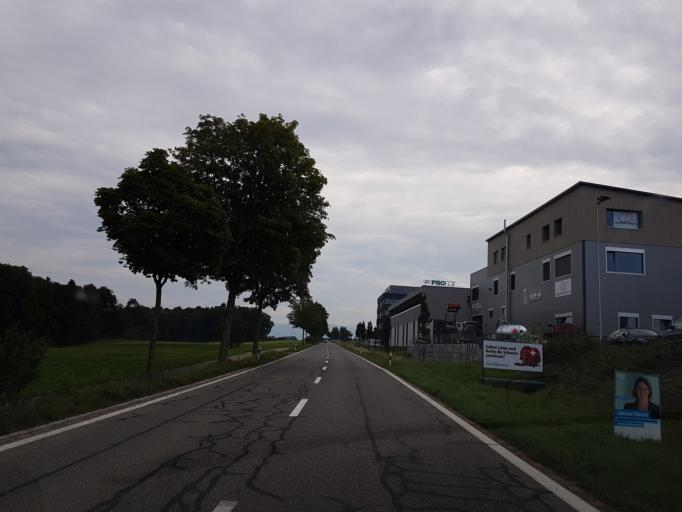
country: CH
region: Aargau
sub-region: Bezirk Muri
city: Muri
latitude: 47.2603
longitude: 8.3534
